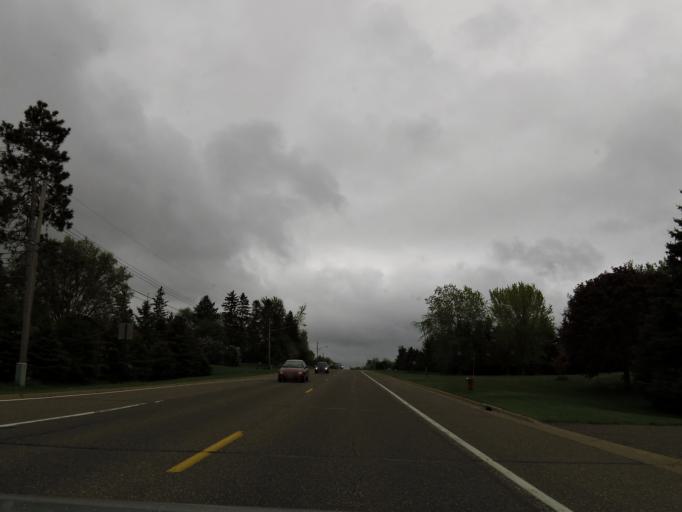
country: US
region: Minnesota
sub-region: Washington County
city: Oakdale
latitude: 44.9900
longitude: -92.9340
